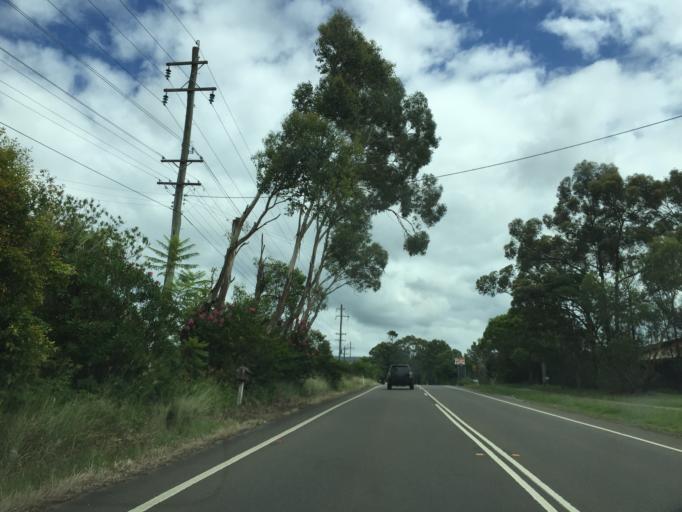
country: AU
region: New South Wales
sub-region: Hawkesbury
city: Richmond
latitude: -33.5570
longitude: 150.6998
